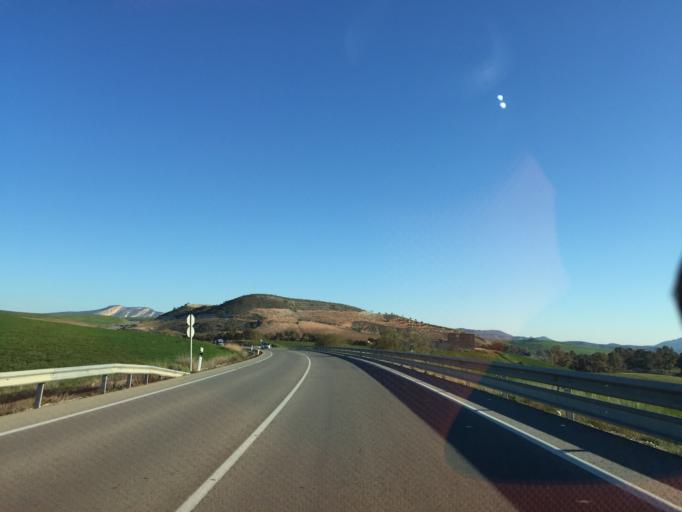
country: ES
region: Andalusia
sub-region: Provincia de Malaga
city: Ardales
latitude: 36.9017
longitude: -4.8407
